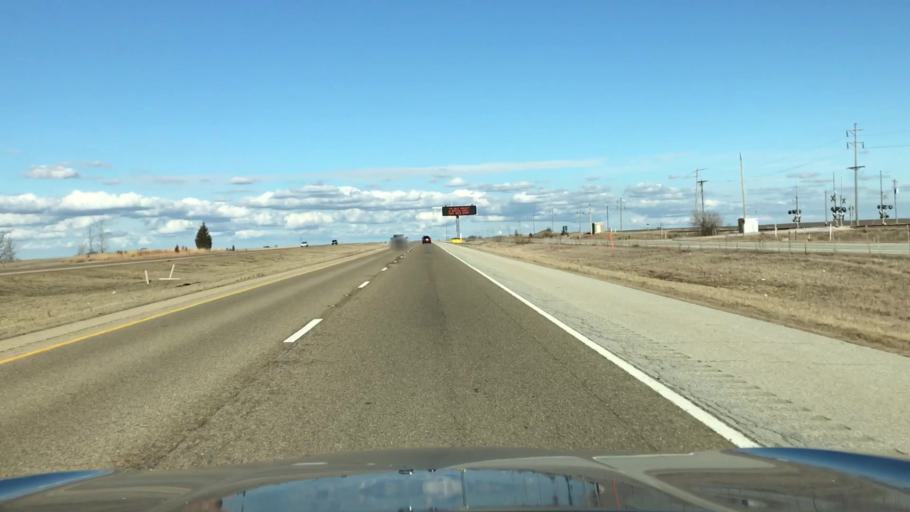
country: US
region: Illinois
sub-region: McLean County
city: Chenoa
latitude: 40.6968
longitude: -88.7515
